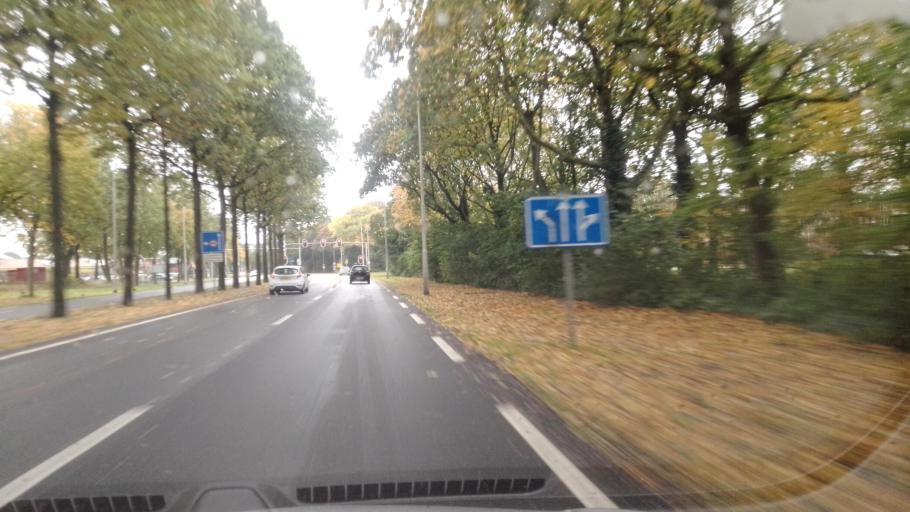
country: NL
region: Limburg
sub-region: Gemeente Venlo
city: Venlo
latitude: 51.3817
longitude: 6.1832
